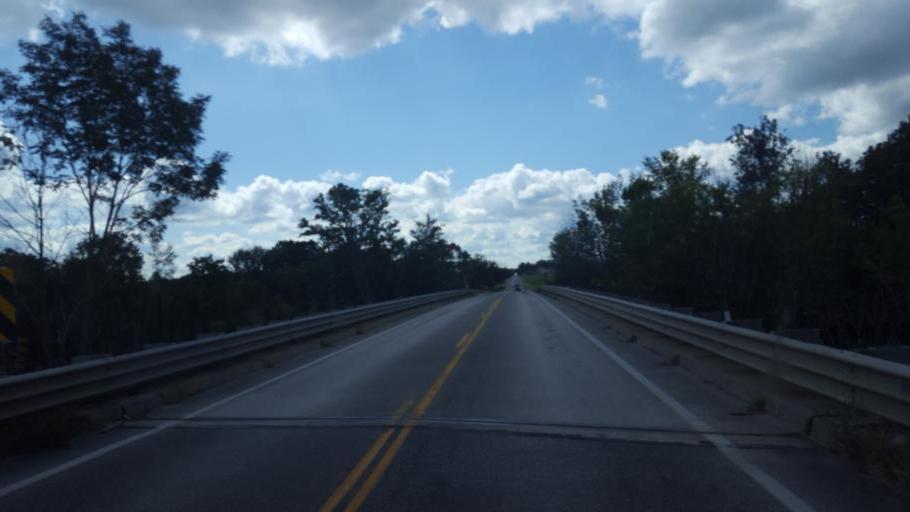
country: US
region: Ohio
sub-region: Wayne County
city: West Salem
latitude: 41.0391
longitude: -82.1260
